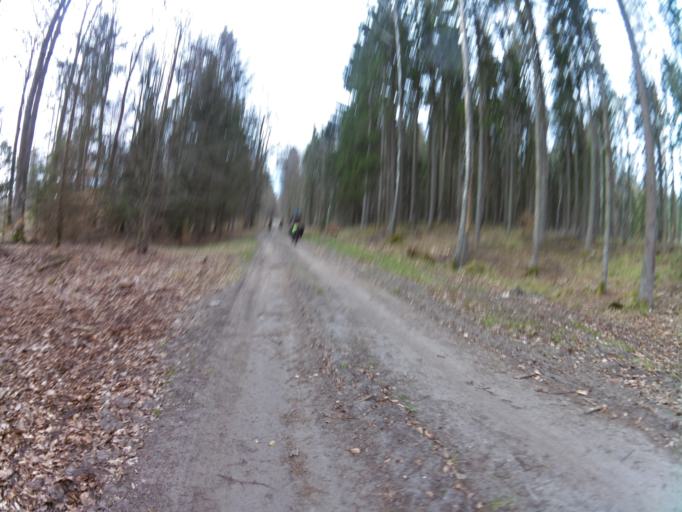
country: PL
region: West Pomeranian Voivodeship
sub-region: Powiat szczecinecki
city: Bialy Bor
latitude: 53.8908
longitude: 16.7184
